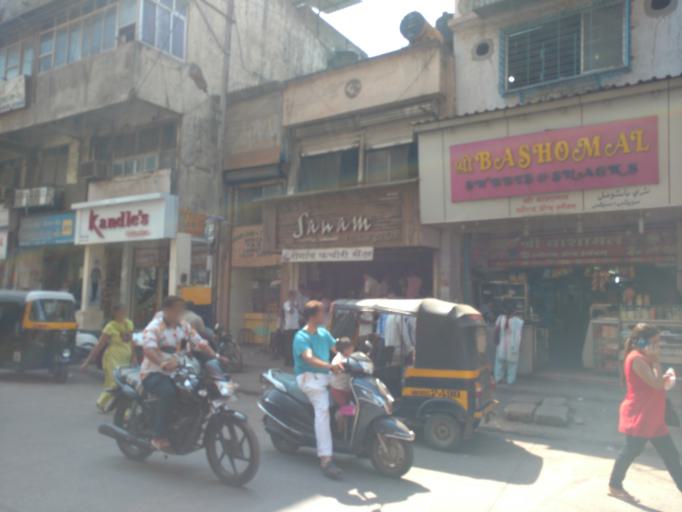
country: IN
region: Maharashtra
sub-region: Thane
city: Ulhasnagar
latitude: 19.2337
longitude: 73.1616
